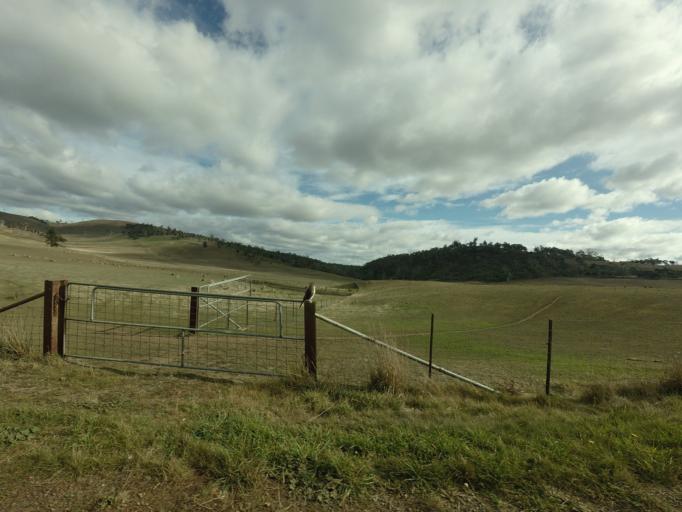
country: AU
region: Tasmania
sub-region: Brighton
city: Bridgewater
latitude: -42.4655
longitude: 147.2787
